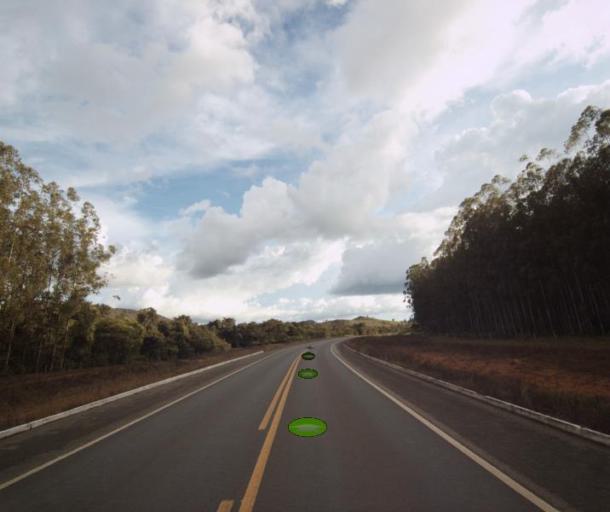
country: BR
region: Goias
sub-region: Niquelandia
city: Niquelandia
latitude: -14.5739
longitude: -48.5654
